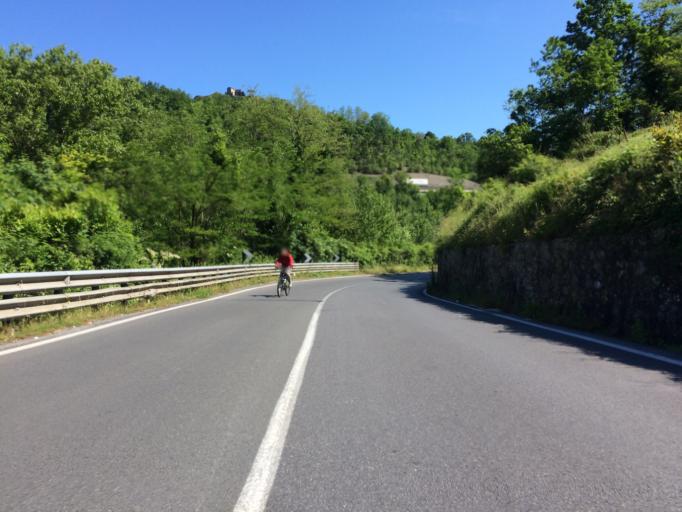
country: IT
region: Tuscany
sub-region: Provincia di Massa-Carrara
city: Montale
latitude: 44.1983
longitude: 9.9521
